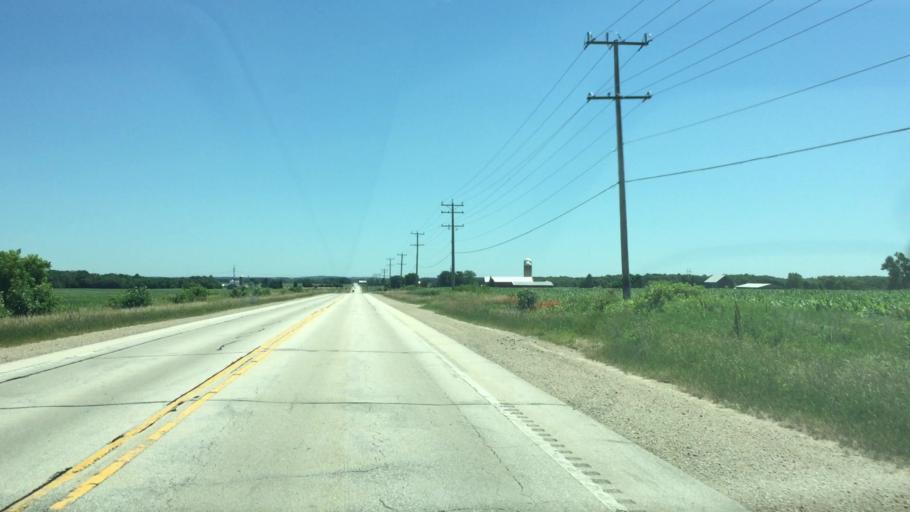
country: US
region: Wisconsin
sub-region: Calumet County
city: Sherwood
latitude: 44.1407
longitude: -88.2330
